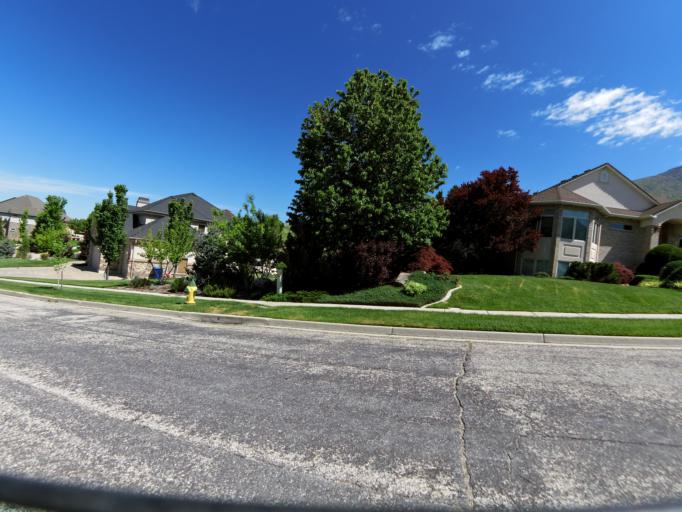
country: US
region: Utah
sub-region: Weber County
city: Uintah
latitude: 41.1741
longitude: -111.9384
